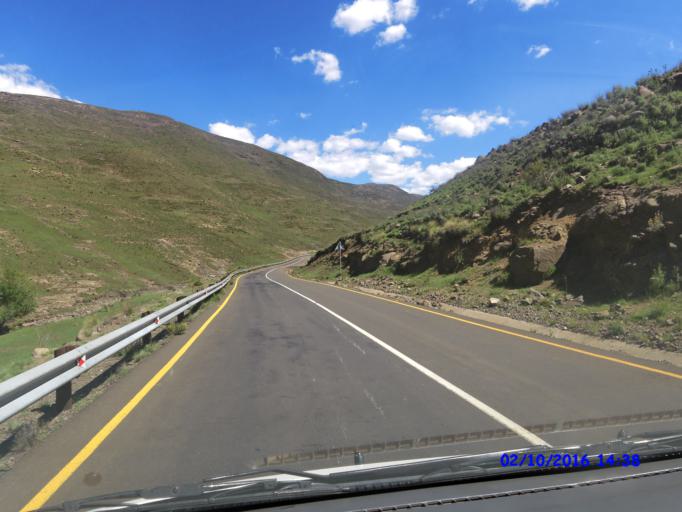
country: LS
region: Maseru
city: Nako
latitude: -29.5067
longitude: 28.0629
